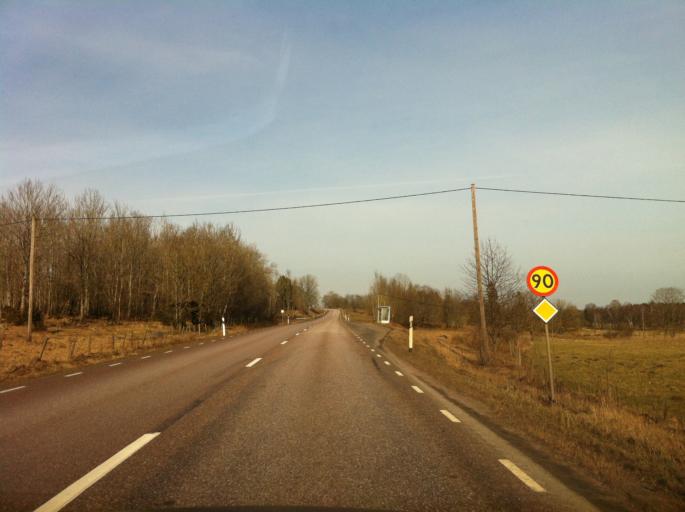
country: SE
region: Vaestra Goetaland
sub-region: Skovde Kommun
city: Skultorp
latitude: 58.2924
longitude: 13.8058
